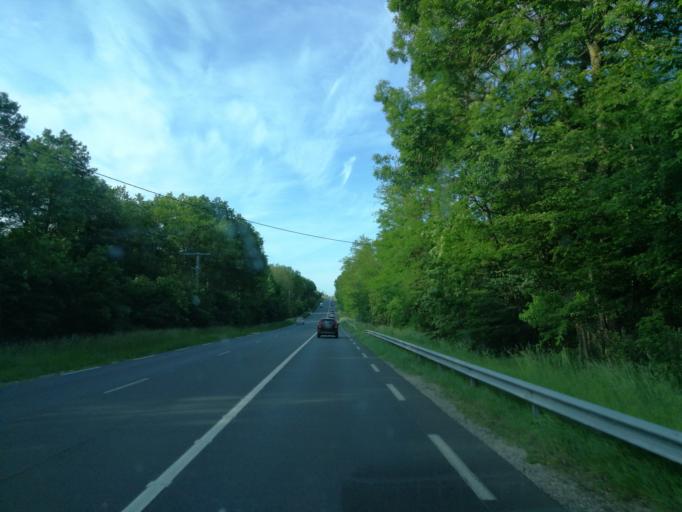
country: FR
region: Centre
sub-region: Departement d'Eure-et-Loir
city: Marboue
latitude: 48.1367
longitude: 1.3429
